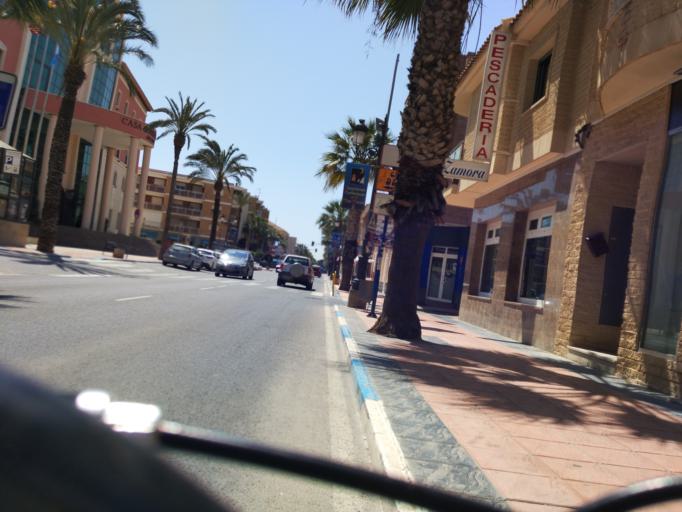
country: ES
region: Murcia
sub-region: Murcia
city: Los Alcazares
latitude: 37.7399
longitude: -0.8519
